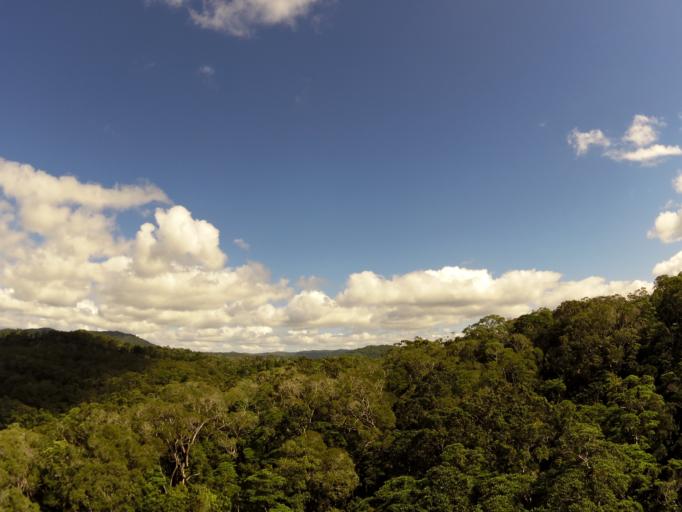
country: AU
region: Queensland
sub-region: Tablelands
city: Kuranda
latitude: -16.8316
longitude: 145.6446
